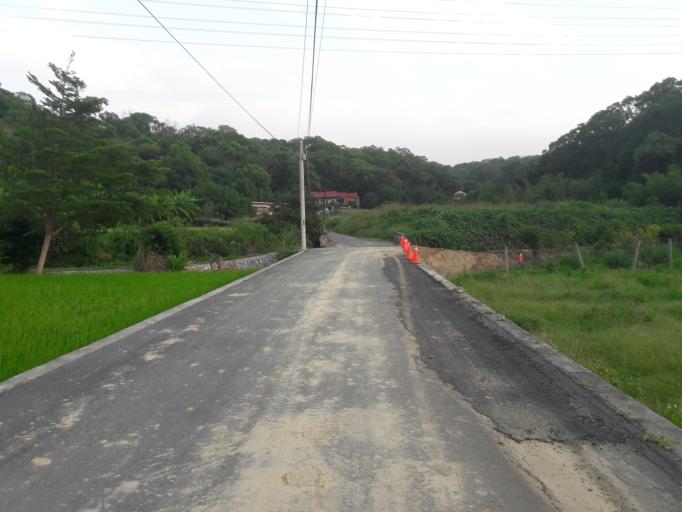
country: TW
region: Taiwan
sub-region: Hsinchu
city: Hsinchu
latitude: 24.7398
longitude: 120.9585
